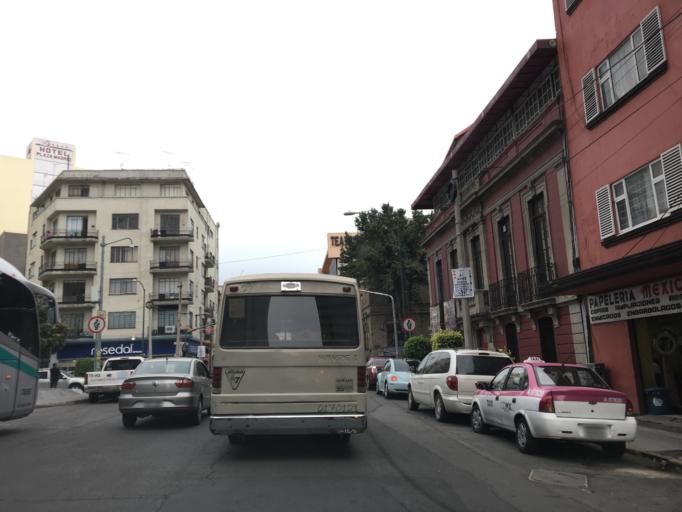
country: MX
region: Mexico City
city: Cuauhtemoc
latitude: 19.4341
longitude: -99.1554
